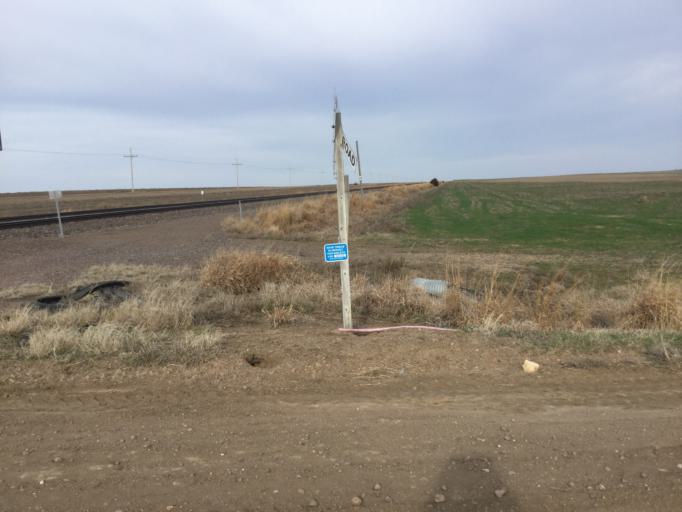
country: US
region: Kansas
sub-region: Ellis County
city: Ellis
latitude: 38.9566
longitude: -99.6691
